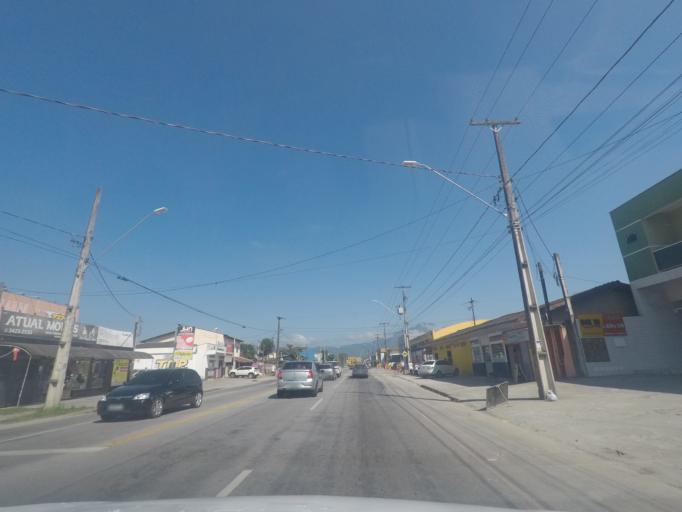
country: BR
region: Parana
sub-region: Paranagua
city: Paranagua
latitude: -25.5647
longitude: -48.5670
